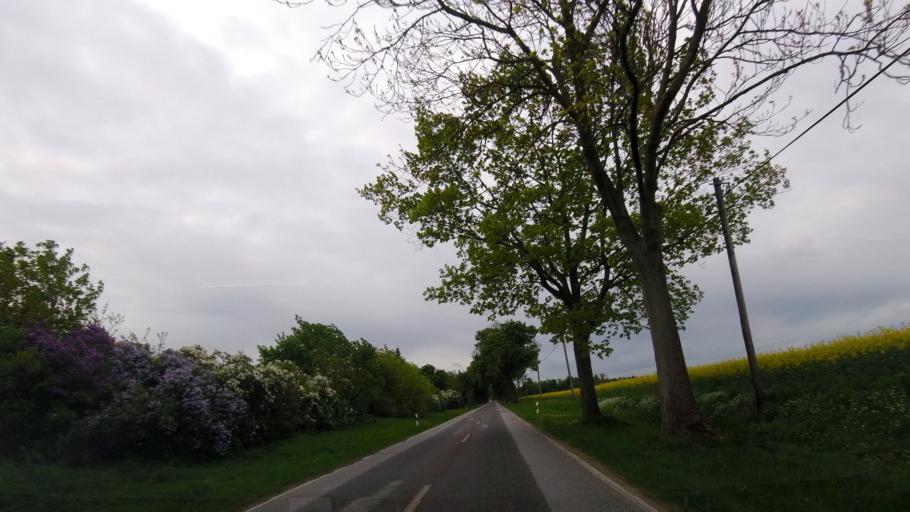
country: DE
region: Brandenburg
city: Dahme
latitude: 51.8796
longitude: 13.4200
